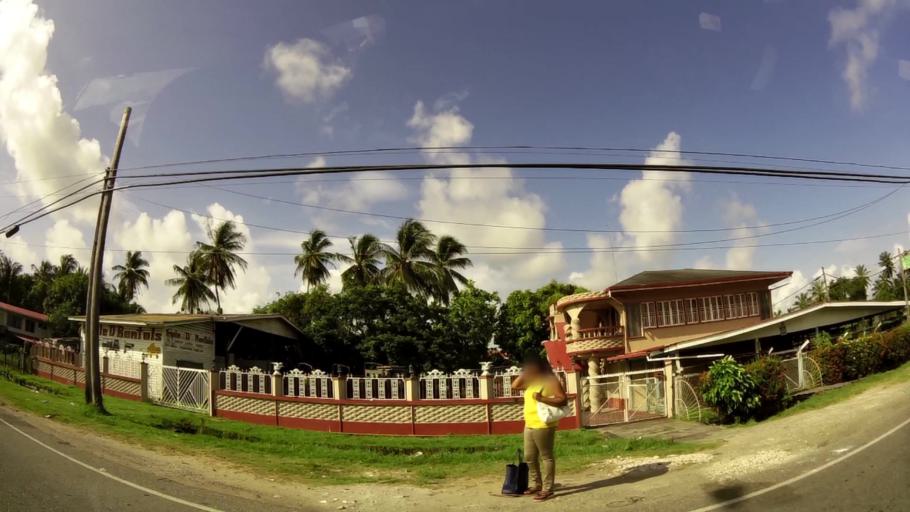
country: GY
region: Demerara-Mahaica
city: Mahaica Village
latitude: 6.7473
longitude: -57.9620
